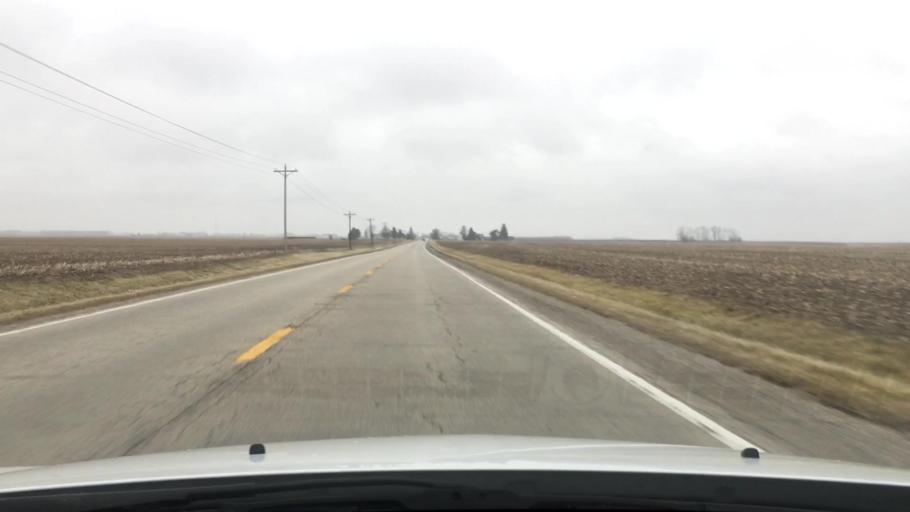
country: US
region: Illinois
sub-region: Iroquois County
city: Watseka
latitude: 40.8906
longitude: -87.6942
